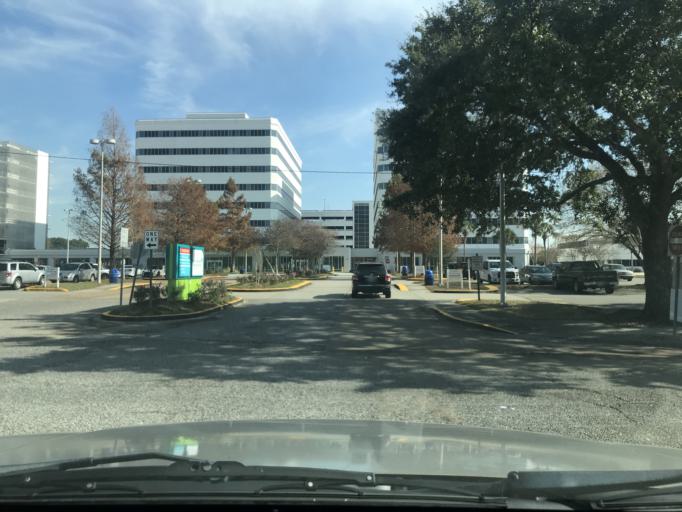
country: US
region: Louisiana
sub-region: Jefferson Parish
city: Marrero
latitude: 29.8903
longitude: -90.0959
